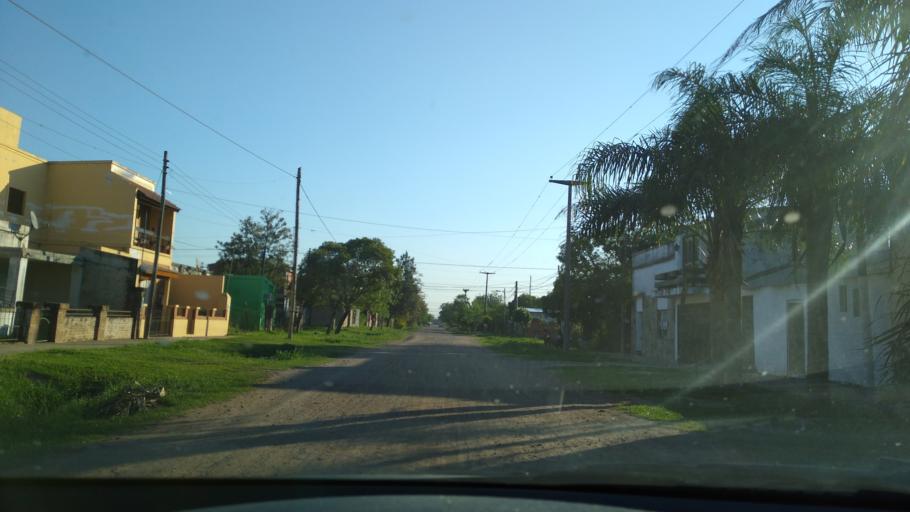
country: AR
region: Chaco
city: Barranqueras
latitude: -27.4904
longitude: -58.9321
